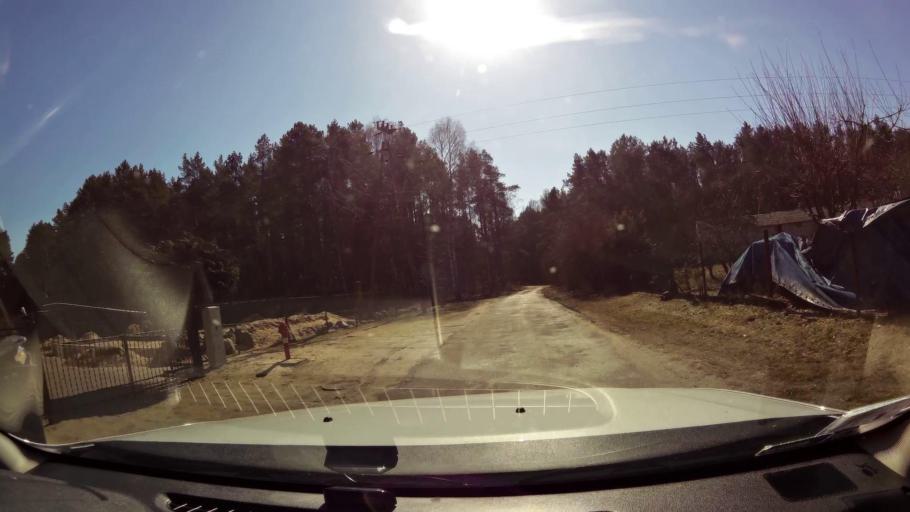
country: PL
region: West Pomeranian Voivodeship
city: Trzcinsko Zdroj
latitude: 53.0334
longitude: 14.6324
